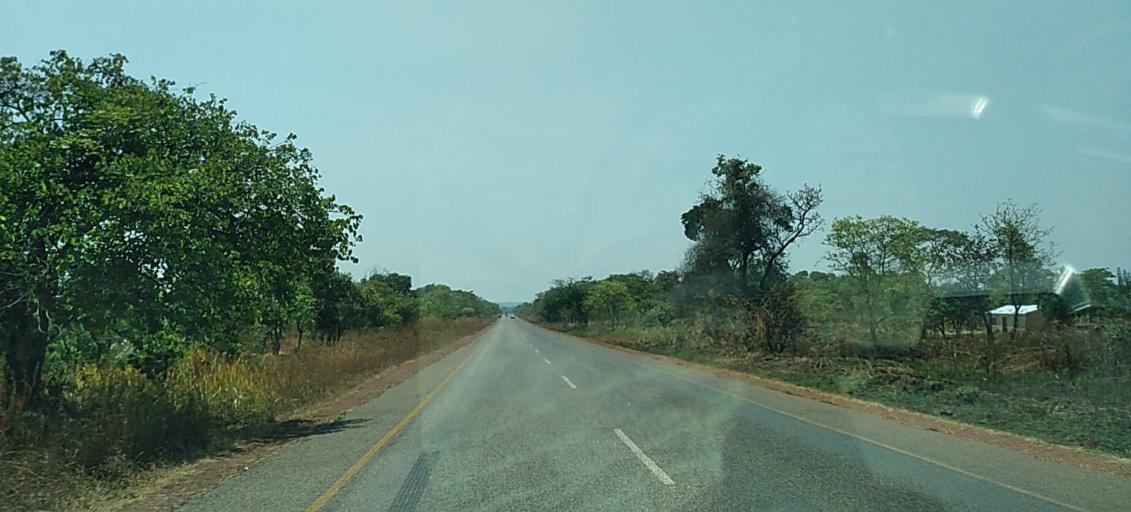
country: ZM
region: North-Western
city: Solwezi
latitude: -12.3929
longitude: 26.2145
